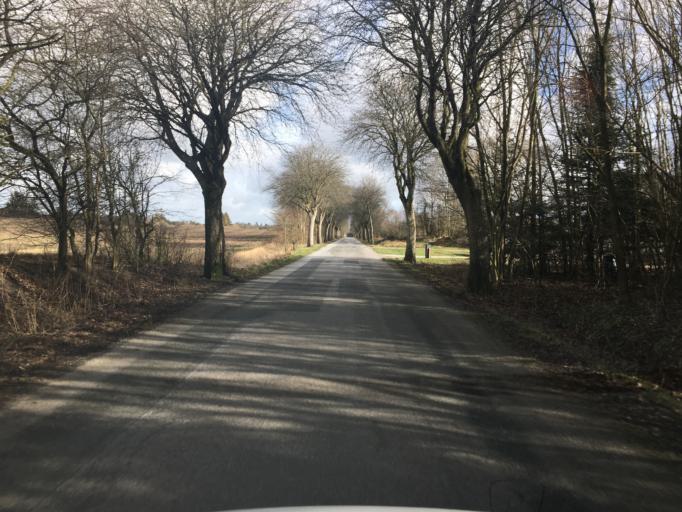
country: DK
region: South Denmark
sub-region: Aabenraa Kommune
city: Krusa
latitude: 54.9010
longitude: 9.4098
